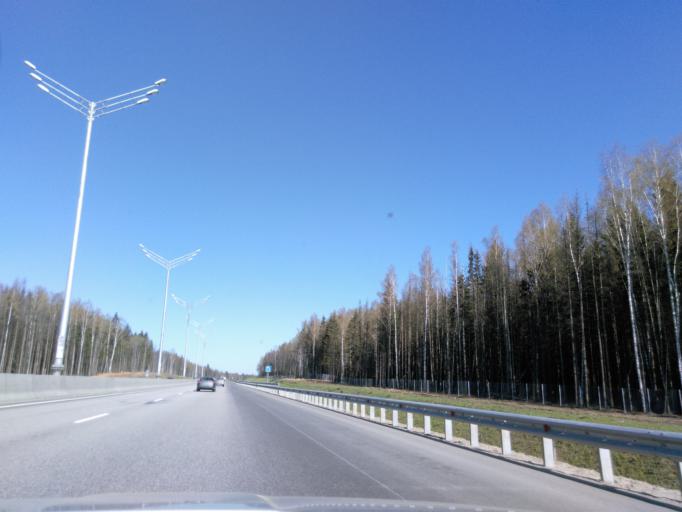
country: RU
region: Moskovskaya
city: Mendeleyevo
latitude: 56.0652
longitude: 37.2319
